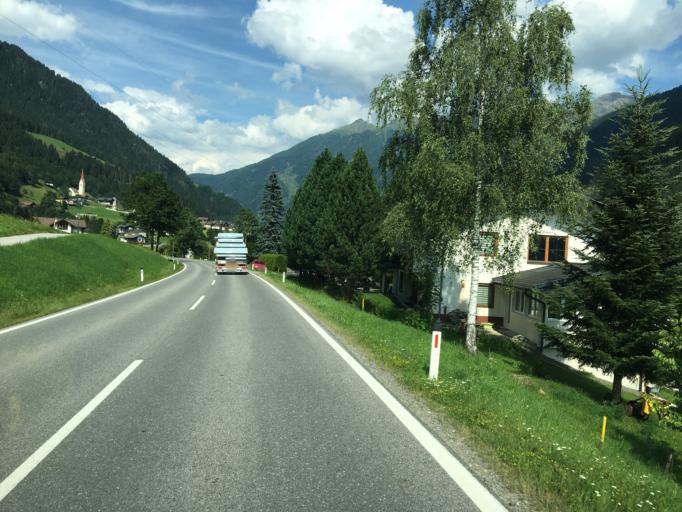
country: AT
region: Carinthia
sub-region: Politischer Bezirk Spittal an der Drau
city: Stall
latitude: 46.8827
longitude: 13.0233
